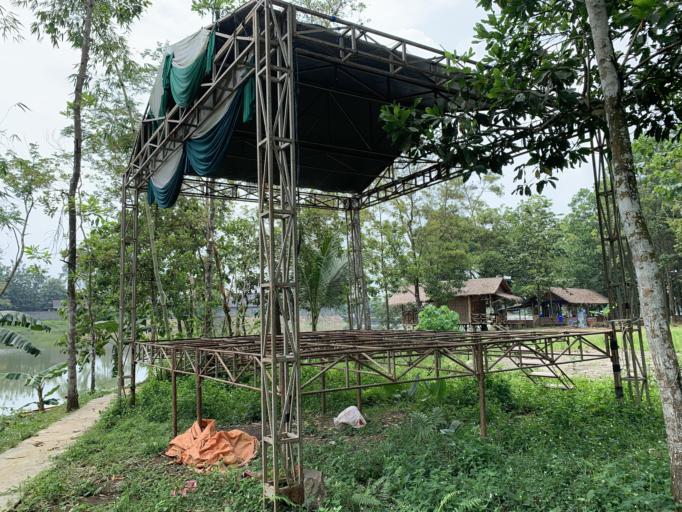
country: ID
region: West Java
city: Serpong
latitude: -6.4086
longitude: 106.5853
